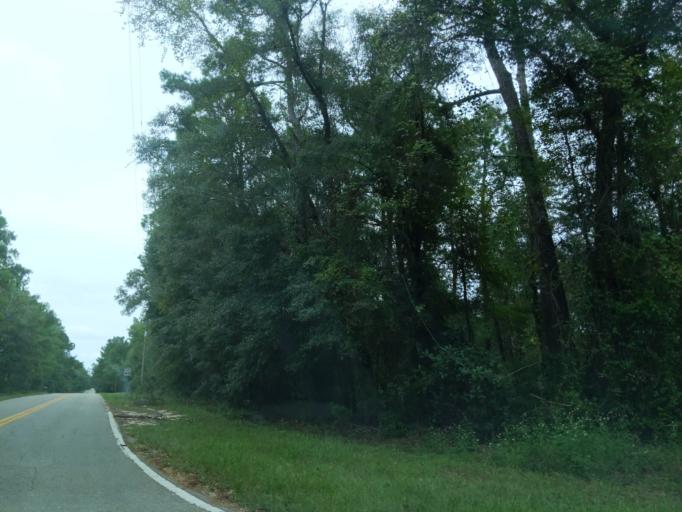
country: US
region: Florida
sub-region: Leon County
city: Woodville
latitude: 30.3677
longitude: -84.1470
